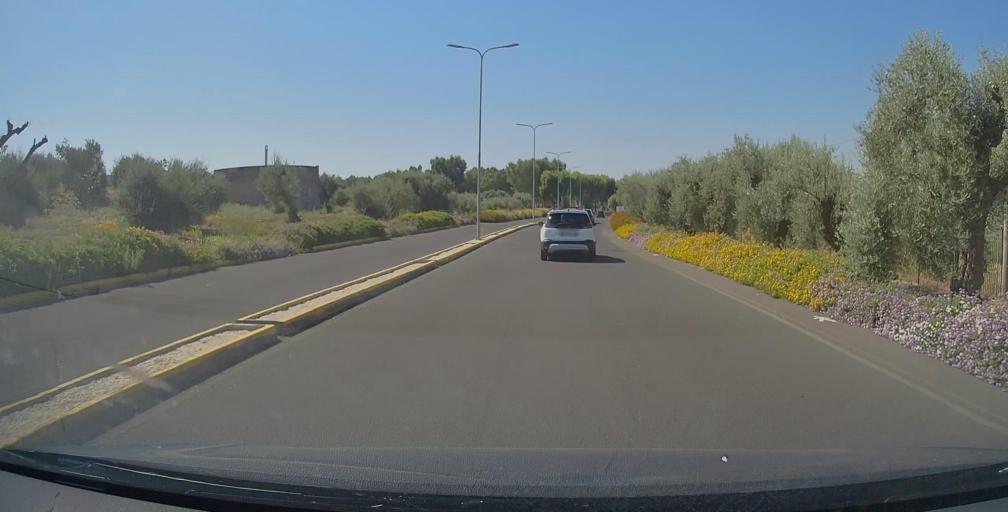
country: IT
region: Sicily
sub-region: Catania
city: Palazzolo
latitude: 37.5402
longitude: 14.9313
